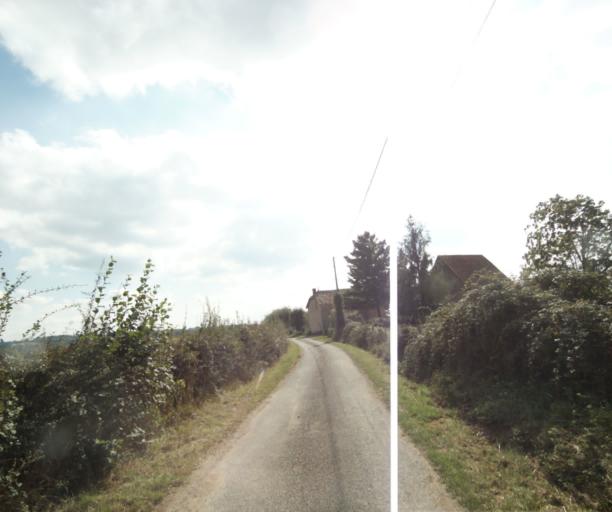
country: FR
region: Bourgogne
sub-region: Departement de Saone-et-Loire
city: Palinges
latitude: 46.4984
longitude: 4.2357
